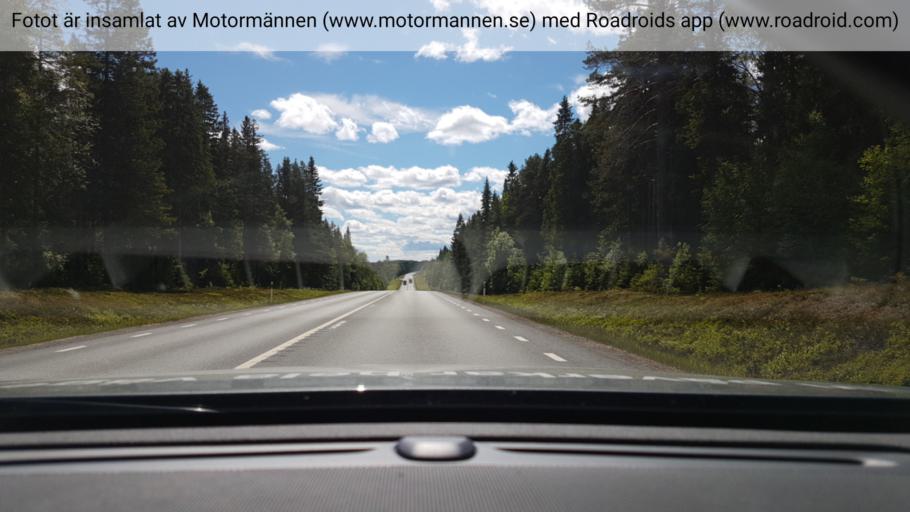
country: SE
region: Vaesterbotten
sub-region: Skelleftea Kommun
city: Burea
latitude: 64.3598
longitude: 21.2962
